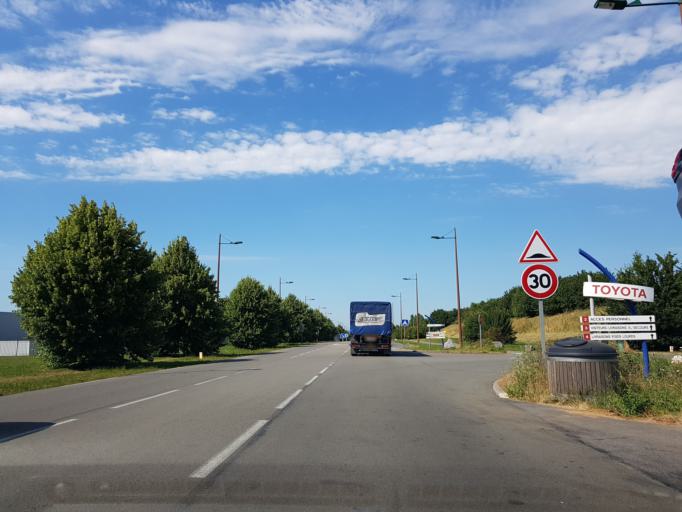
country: FR
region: Nord-Pas-de-Calais
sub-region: Departement du Nord
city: Onnaing
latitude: 50.3636
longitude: 3.6091
